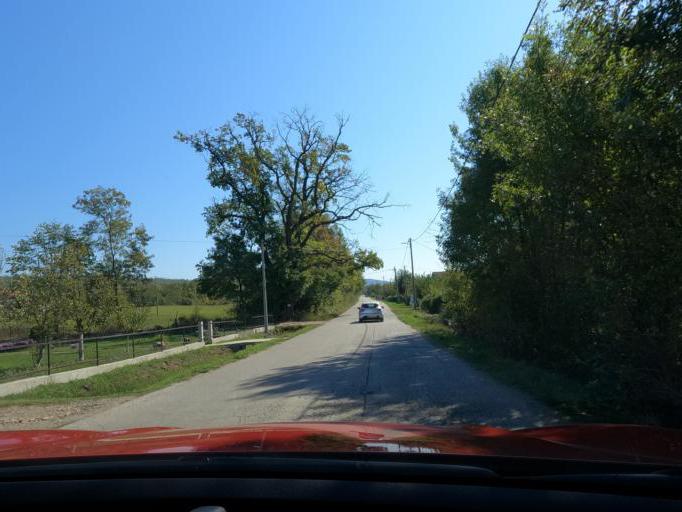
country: RS
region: Central Serbia
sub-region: Raski Okrug
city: Kraljevo
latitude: 43.7554
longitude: 20.6917
